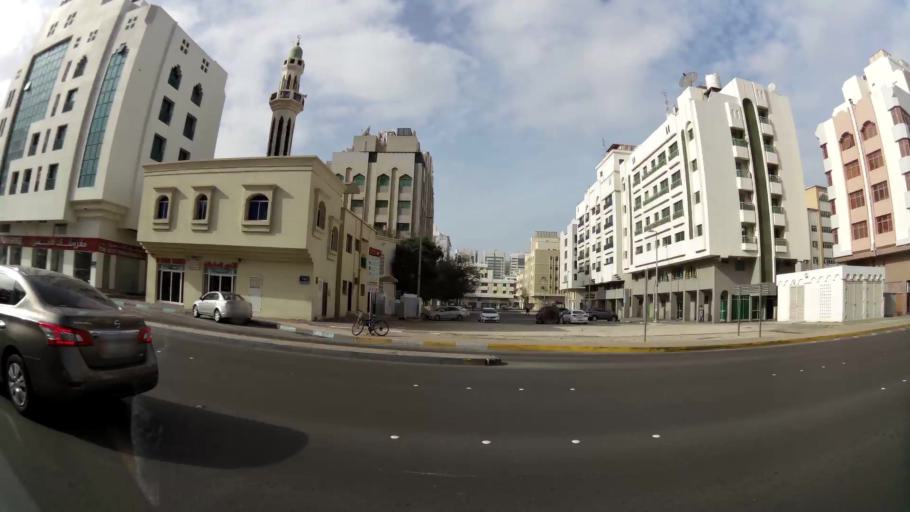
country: AE
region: Abu Dhabi
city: Abu Dhabi
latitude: 24.4626
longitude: 54.3855
